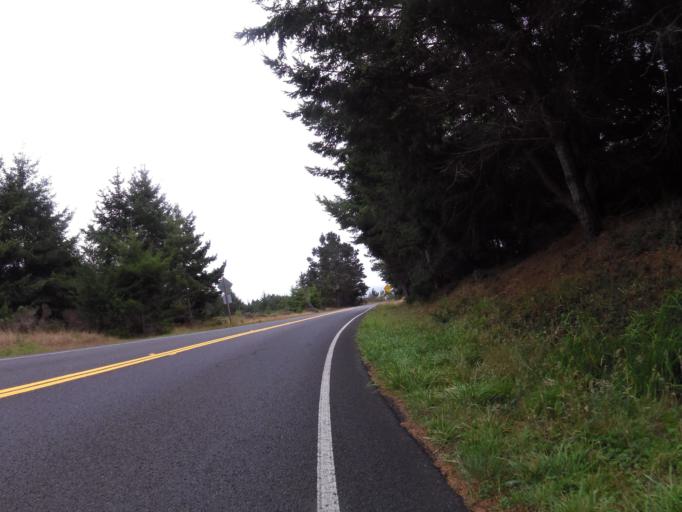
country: US
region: California
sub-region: Sonoma County
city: Monte Rio
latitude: 38.5174
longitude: -123.2436
